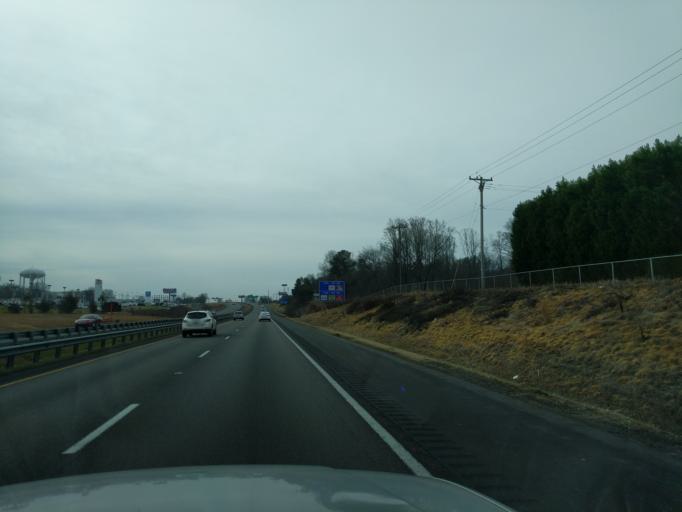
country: US
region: North Carolina
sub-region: Iredell County
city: Statesville
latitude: 35.7831
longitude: -80.8634
